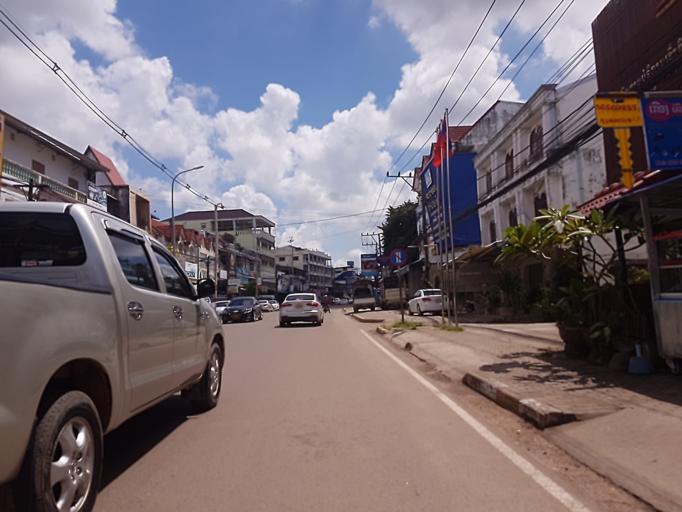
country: LA
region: Vientiane
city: Vientiane
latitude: 17.9633
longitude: 102.6210
